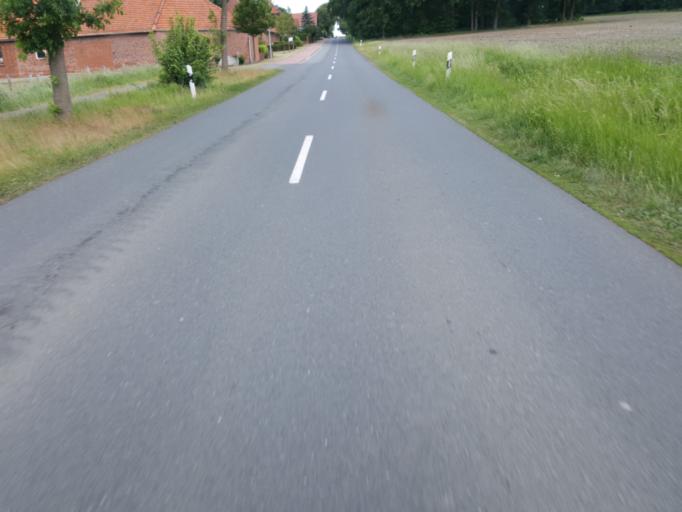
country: DE
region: Lower Saxony
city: Husum
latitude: 52.5761
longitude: 9.2480
